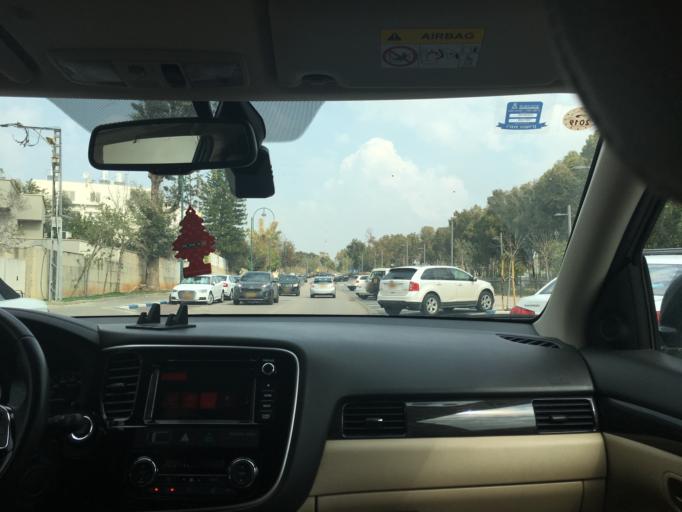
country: IL
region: Tel Aviv
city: Ramat HaSharon
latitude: 32.1389
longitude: 34.8448
